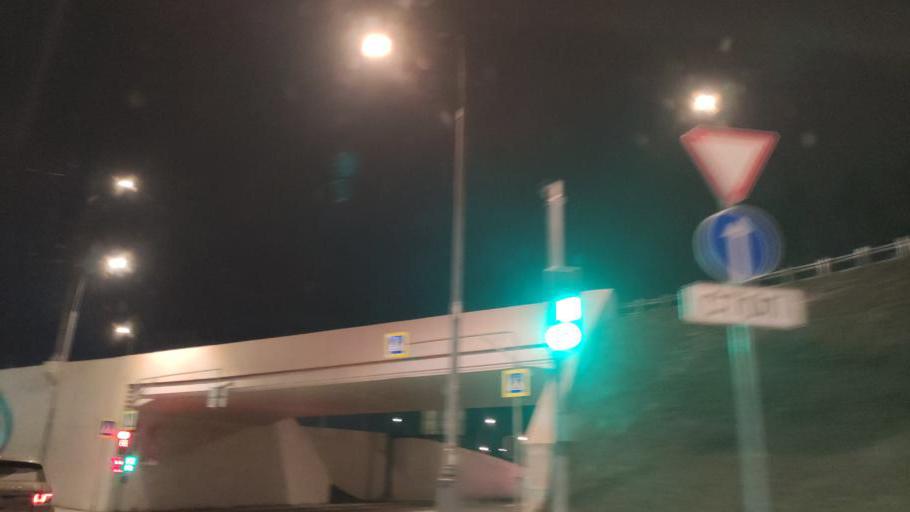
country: RU
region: Moscow
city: Solntsevo
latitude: 55.6220
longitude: 37.4192
